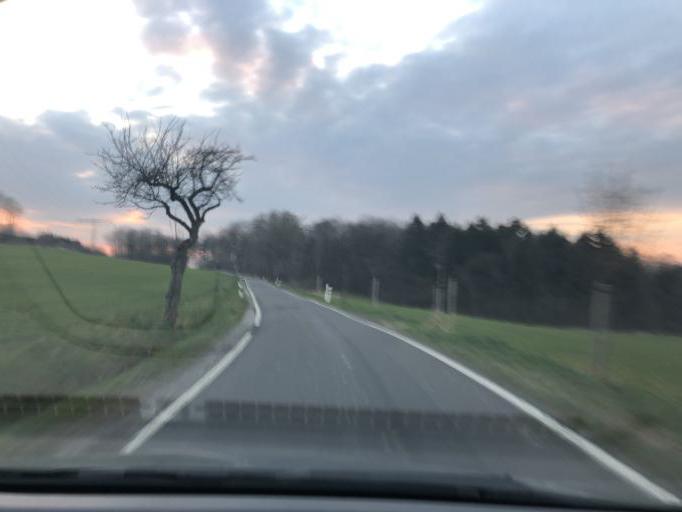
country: DE
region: Saxony
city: Kamenz
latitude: 51.2414
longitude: 14.0764
